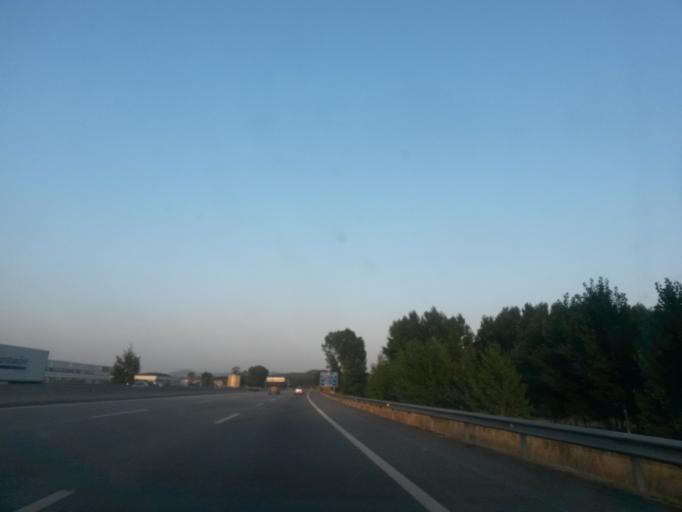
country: ES
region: Catalonia
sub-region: Provincia de Girona
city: Hostalric
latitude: 41.7418
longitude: 2.6531
